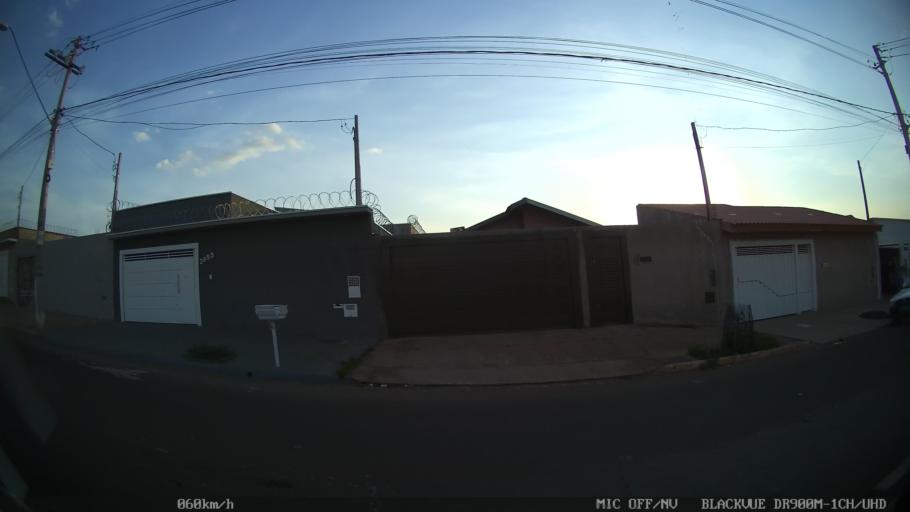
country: BR
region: Sao Paulo
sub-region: Ribeirao Preto
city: Ribeirao Preto
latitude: -21.1382
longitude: -47.8578
